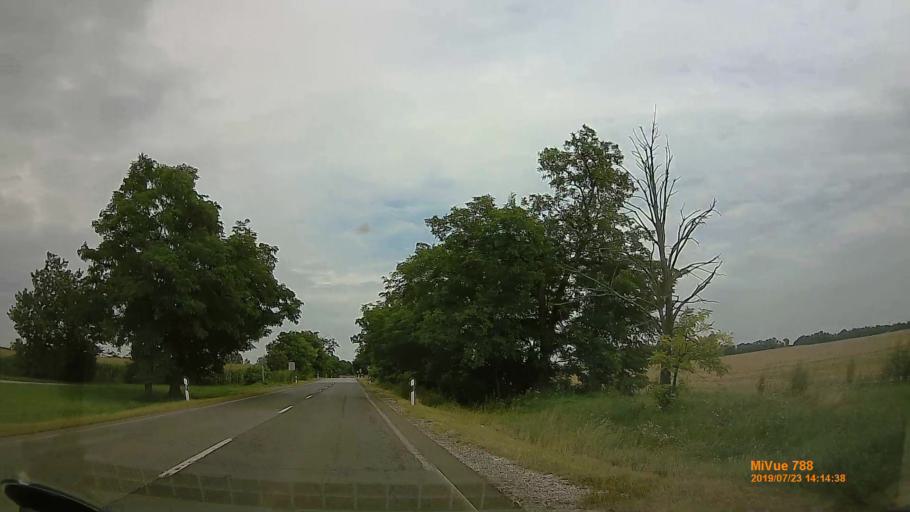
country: HU
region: Szabolcs-Szatmar-Bereg
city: Nagycserkesz
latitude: 47.9572
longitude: 21.4974
